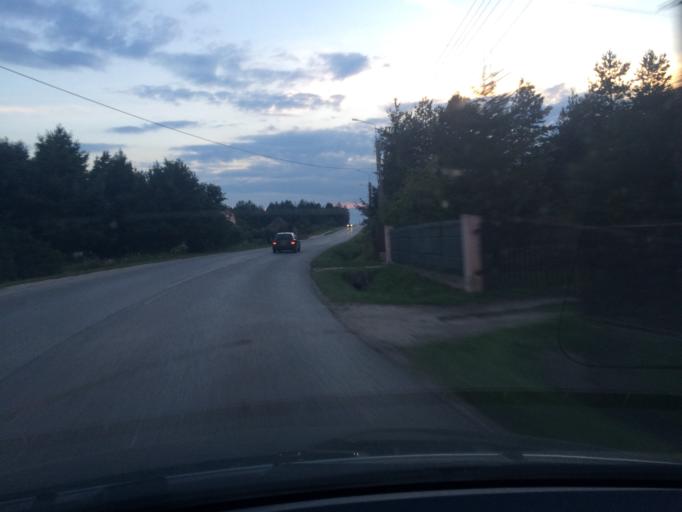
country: PL
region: Swietokrzyskie
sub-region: Powiat skarzyski
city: Suchedniow
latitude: 51.0455
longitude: 20.8828
